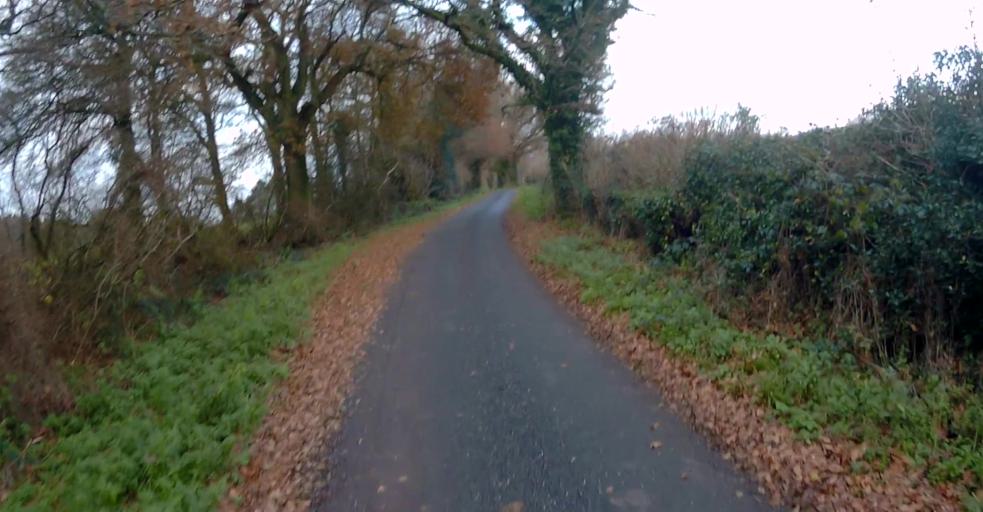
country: GB
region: England
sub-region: Hampshire
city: Basingstoke
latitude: 51.1838
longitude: -1.0982
